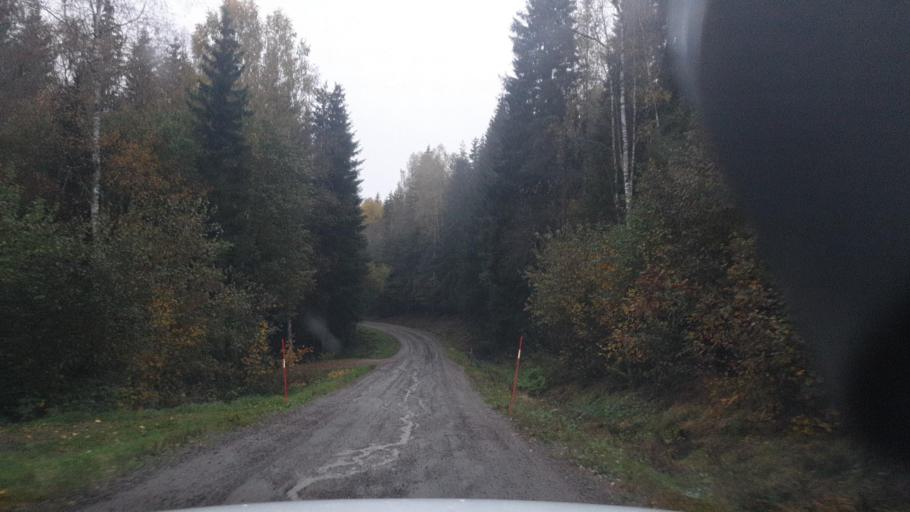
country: SE
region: Vaermland
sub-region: Eda Kommun
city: Amotfors
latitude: 59.8230
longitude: 12.4498
